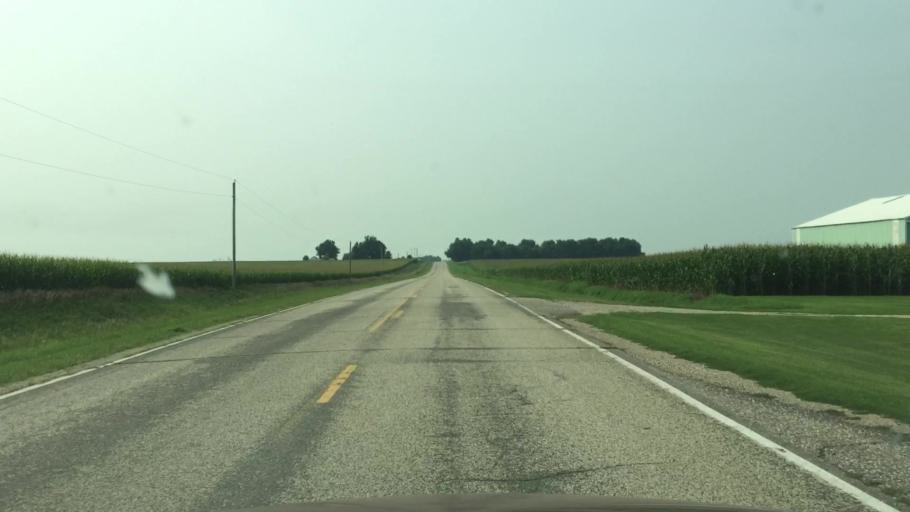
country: US
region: Iowa
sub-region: O'Brien County
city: Sheldon
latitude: 43.2696
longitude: -95.7829
